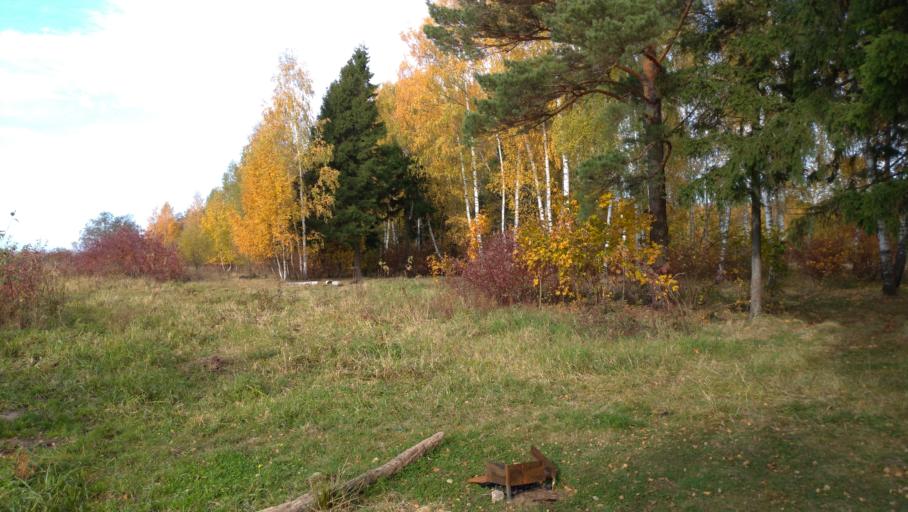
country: RU
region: Moskovskaya
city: Marfino
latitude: 56.1021
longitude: 37.6383
